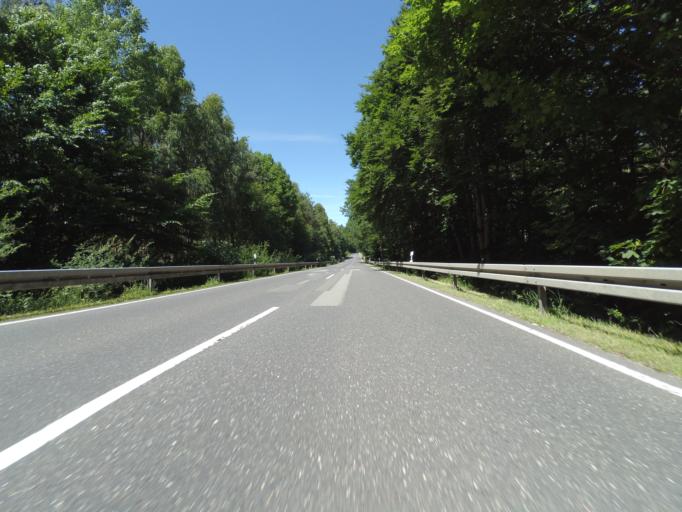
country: DE
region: Mecklenburg-Vorpommern
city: Plau am See
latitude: 53.3971
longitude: 12.2887
